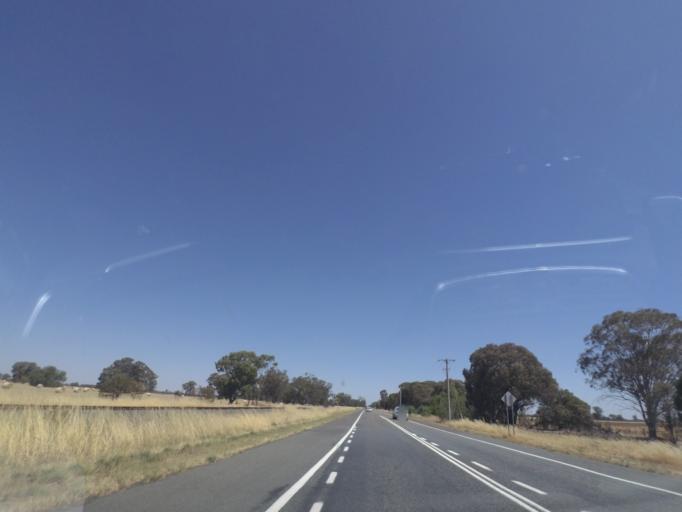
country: AU
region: Victoria
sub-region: Greater Shepparton
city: Shepparton
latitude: -36.1960
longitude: 145.4319
